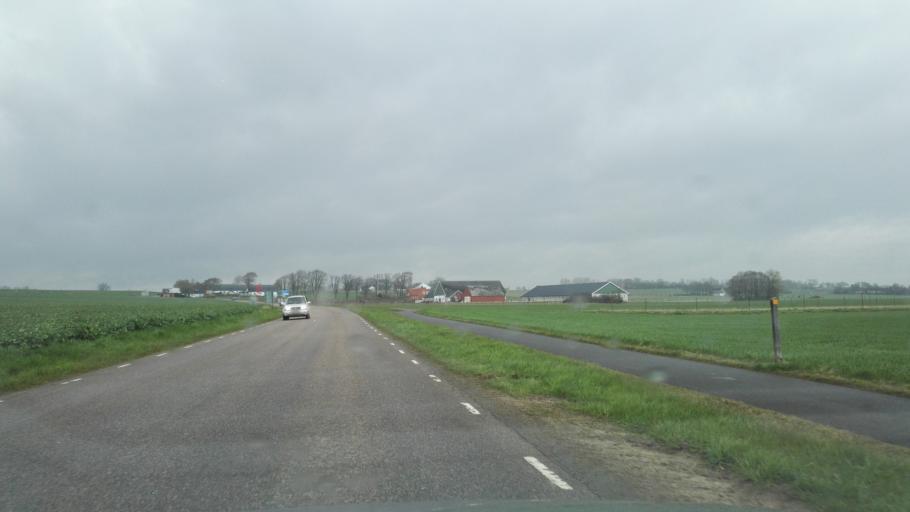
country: SE
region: Skane
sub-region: Simrishamns Kommun
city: Simrishamn
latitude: 55.4797
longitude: 14.2843
